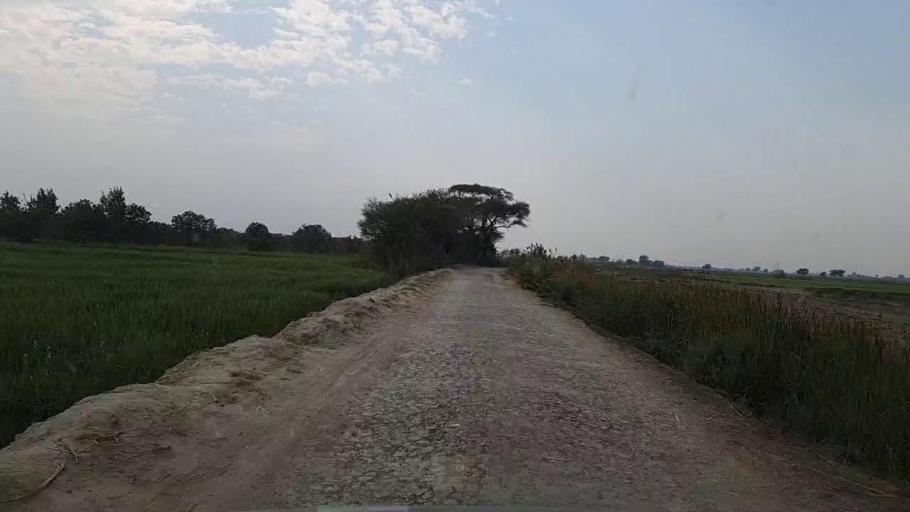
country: PK
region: Sindh
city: Mirwah Gorchani
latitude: 25.3717
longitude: 69.0767
